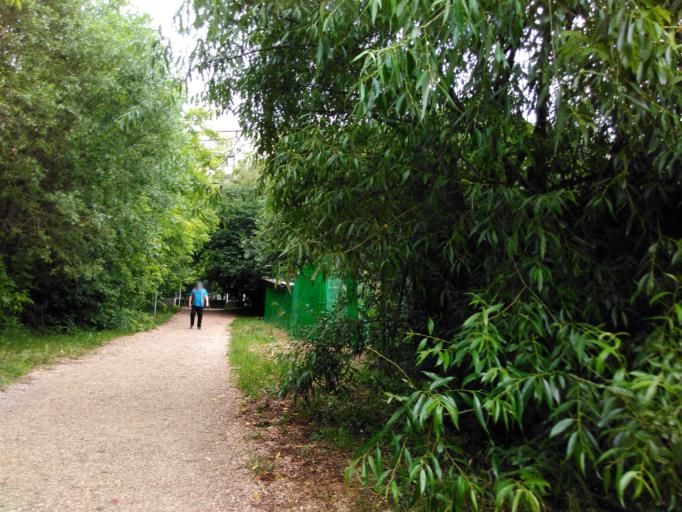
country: RU
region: Moscow
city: Yasenevo
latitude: 55.6312
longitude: 37.5346
